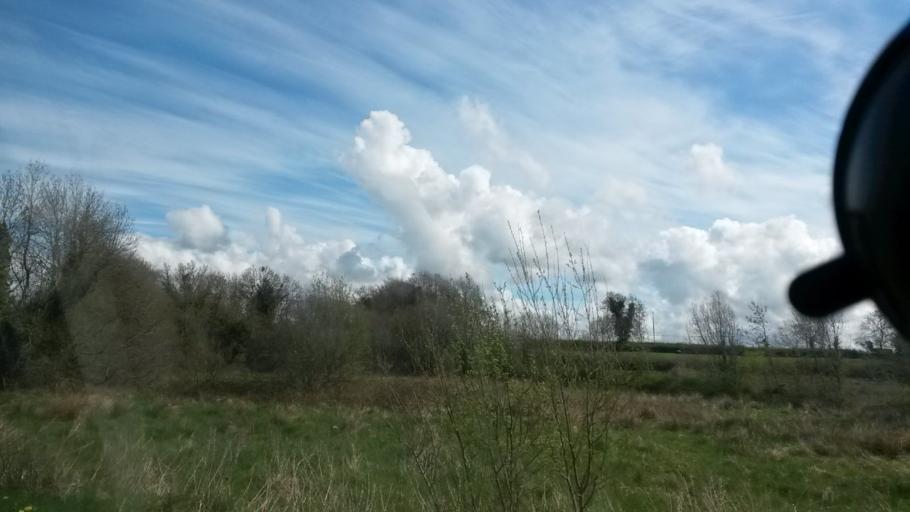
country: IE
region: Ulster
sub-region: An Cabhan
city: Belturbet
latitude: 54.1710
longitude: -7.5049
